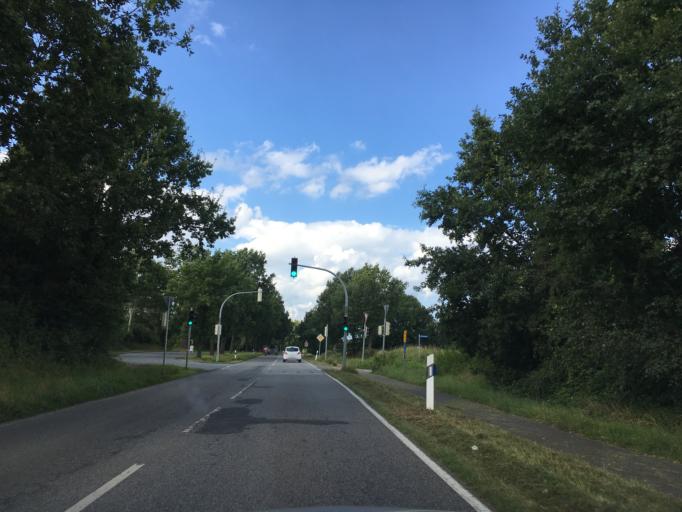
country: DE
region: Schleswig-Holstein
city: Laboe
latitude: 54.4031
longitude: 10.2347
